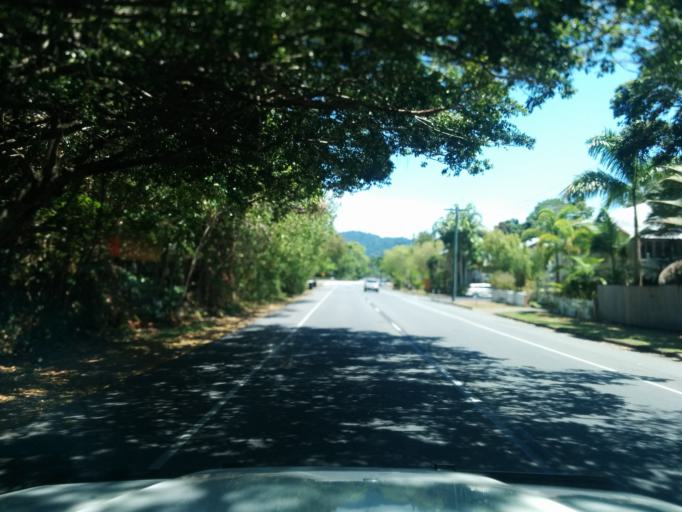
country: AU
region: Queensland
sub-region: Cairns
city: Cairns
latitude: -16.9198
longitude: 145.7599
